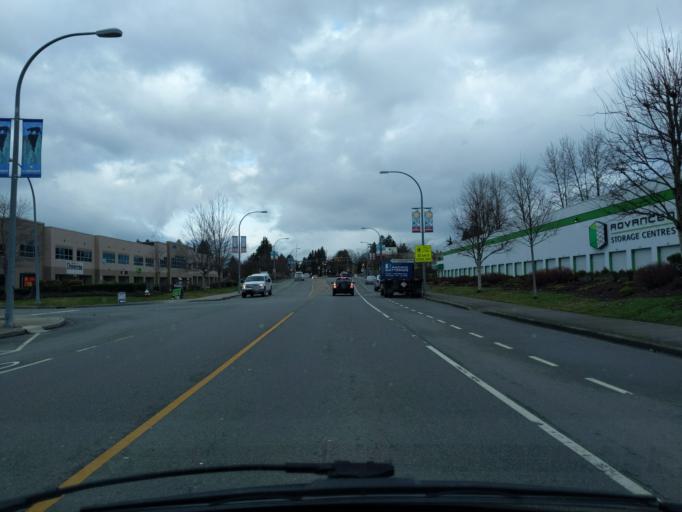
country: CA
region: British Columbia
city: Pitt Meadows
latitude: 49.2103
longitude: -122.6596
